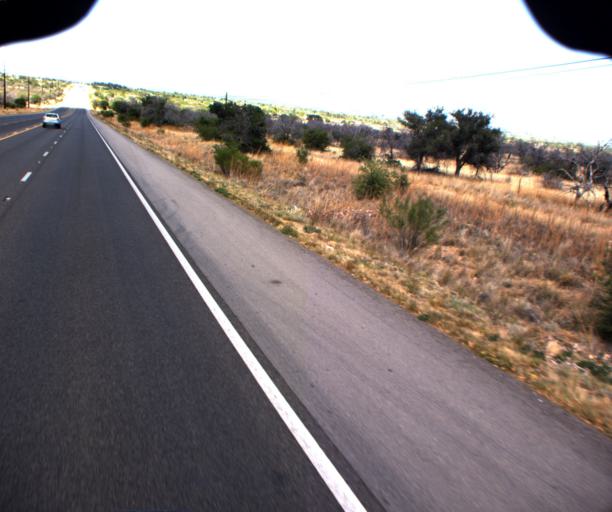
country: US
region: Arizona
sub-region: Cochise County
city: Sierra Vista Southeast
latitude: 31.4104
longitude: -110.2407
